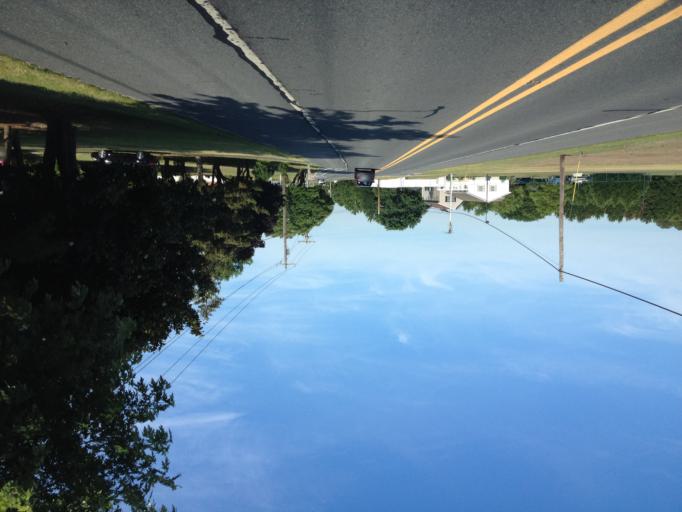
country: US
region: Delaware
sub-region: Sussex County
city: Millsboro
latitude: 38.5446
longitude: -75.2286
